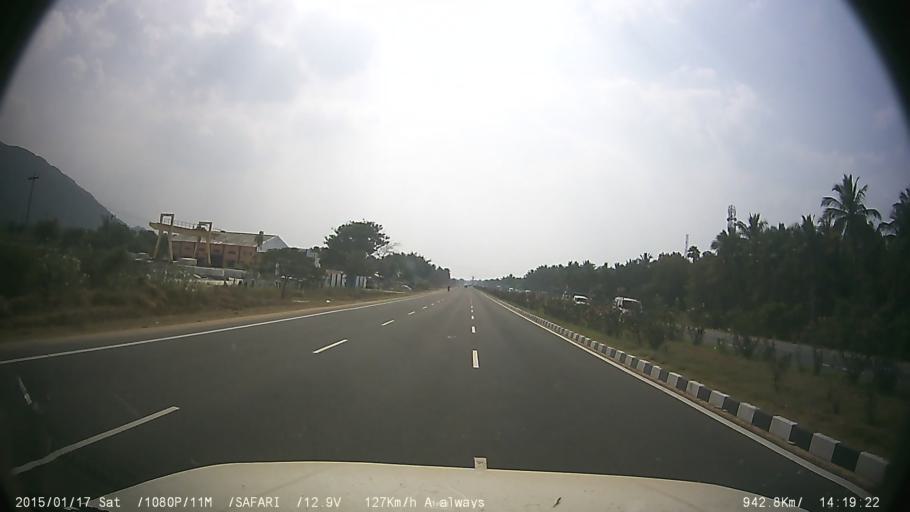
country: IN
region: Tamil Nadu
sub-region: Vellore
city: Vaniyambadi
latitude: 12.7213
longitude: 78.6655
